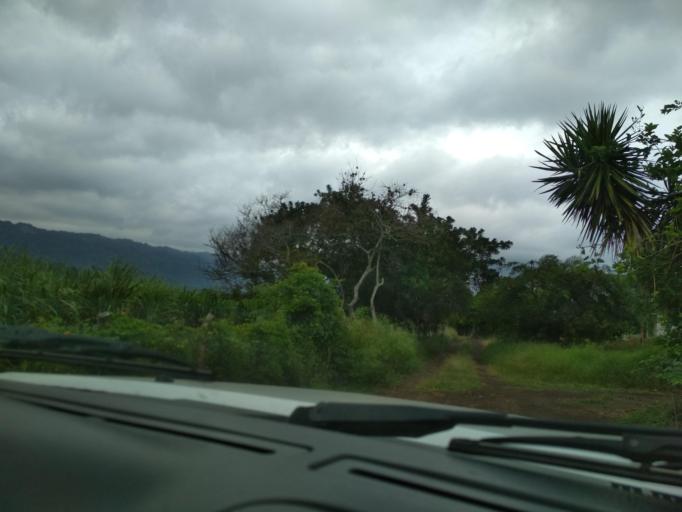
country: MX
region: Veracruz
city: El Castillo
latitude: 19.5862
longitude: -96.8410
